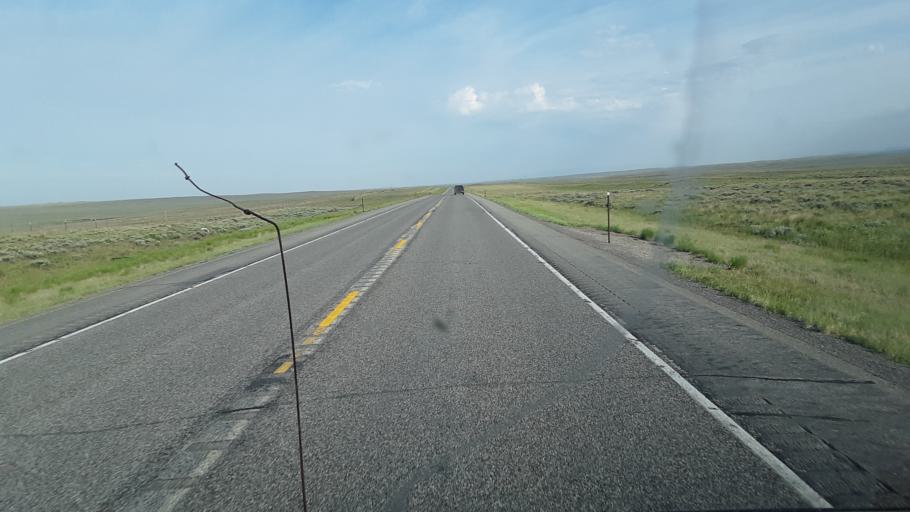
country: US
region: Wyoming
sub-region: Natrona County
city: Mills
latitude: 43.0859
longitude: -107.3066
